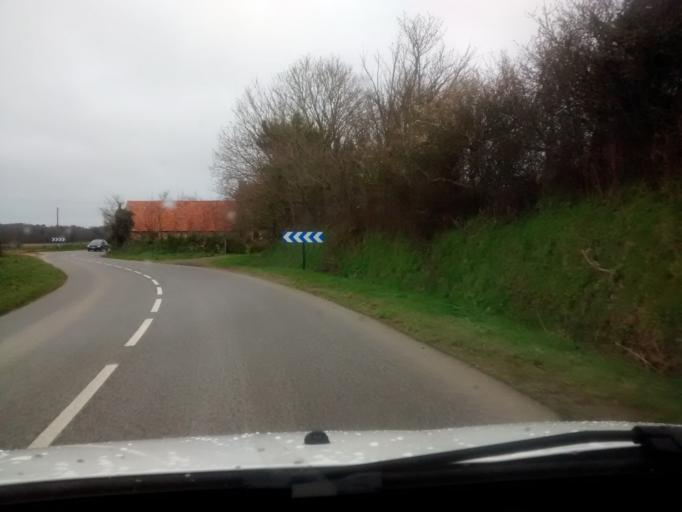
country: FR
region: Brittany
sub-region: Departement des Cotes-d'Armor
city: Plouguiel
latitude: 48.8116
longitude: -3.2372
